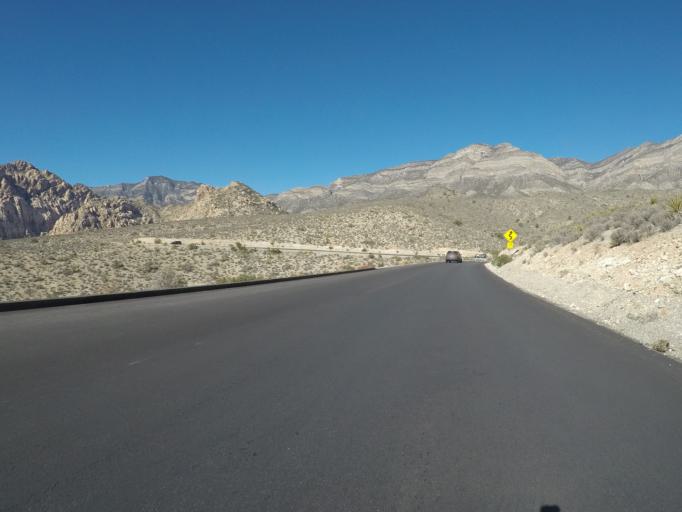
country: US
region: Nevada
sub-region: Clark County
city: Summerlin South
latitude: 36.1710
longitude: -115.4665
